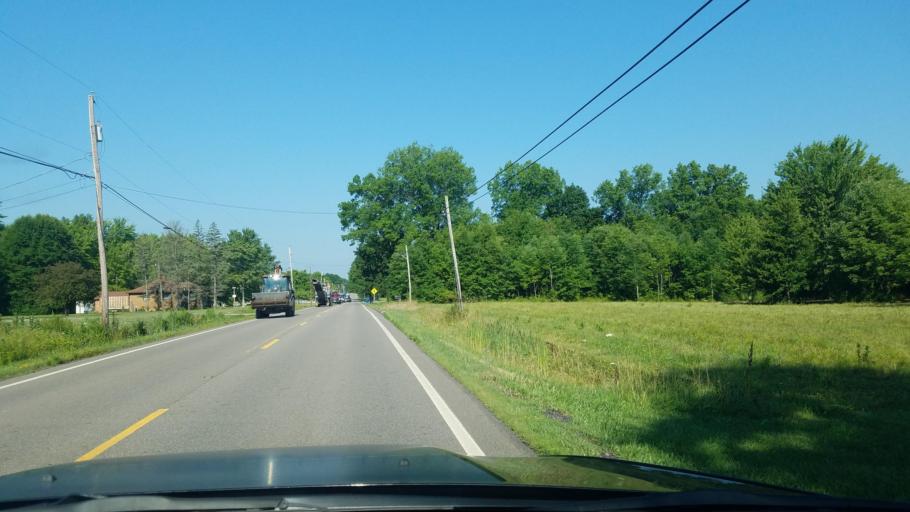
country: US
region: Ohio
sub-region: Trumbull County
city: Champion Heights
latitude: 41.3084
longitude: -80.8610
